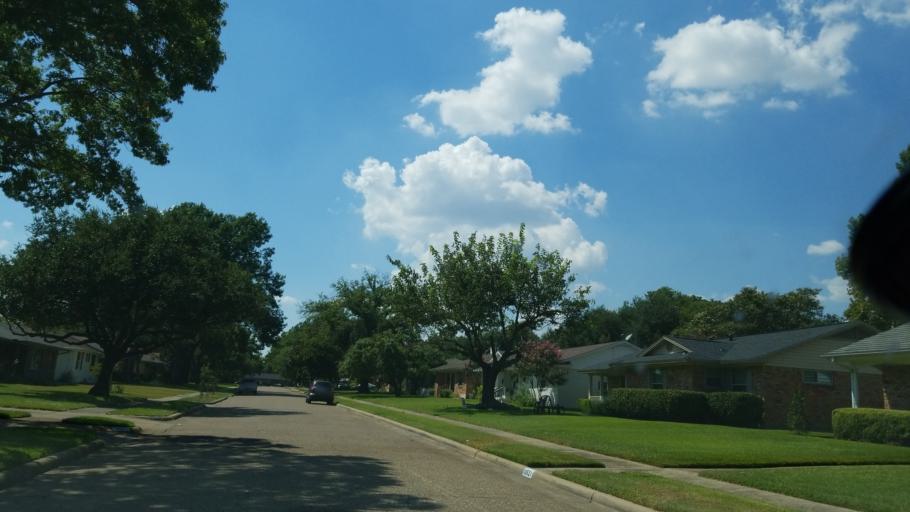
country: US
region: Texas
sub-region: Dallas County
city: Richardson
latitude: 32.8837
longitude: -96.7031
